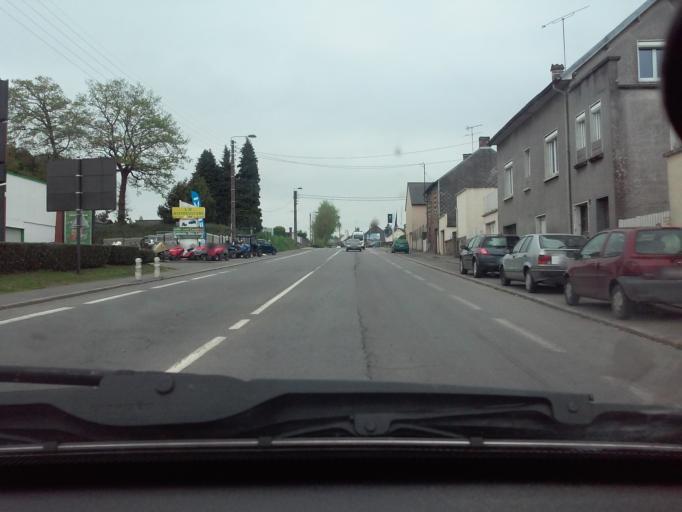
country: FR
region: Brittany
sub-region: Departement d'Ille-et-Vilaine
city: Fougeres
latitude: 48.3452
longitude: -1.1810
